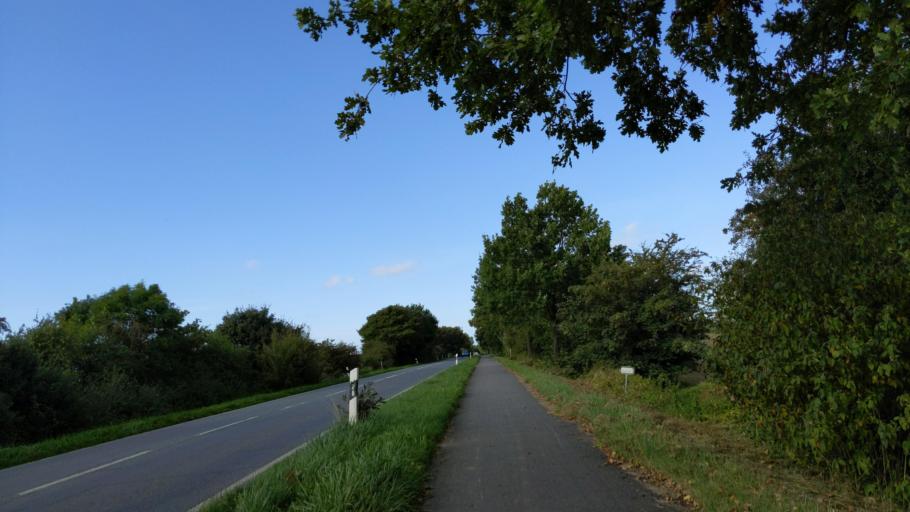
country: DE
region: Schleswig-Holstein
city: Stockelsdorf
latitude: 53.9400
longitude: 10.6304
